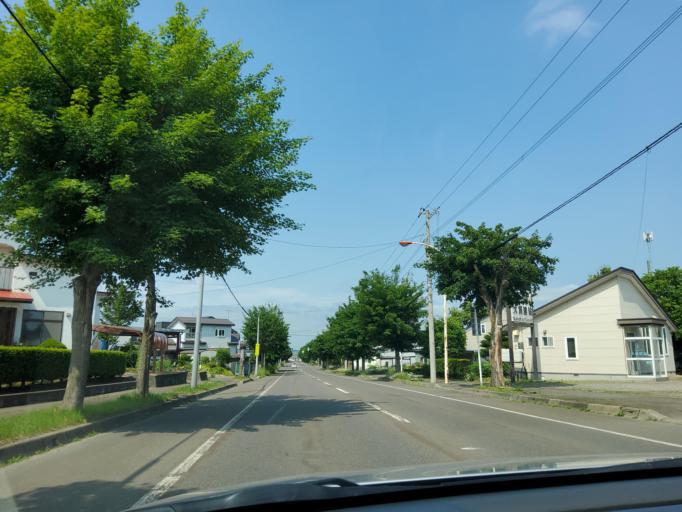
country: JP
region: Hokkaido
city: Obihiro
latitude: 42.9048
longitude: 143.0511
